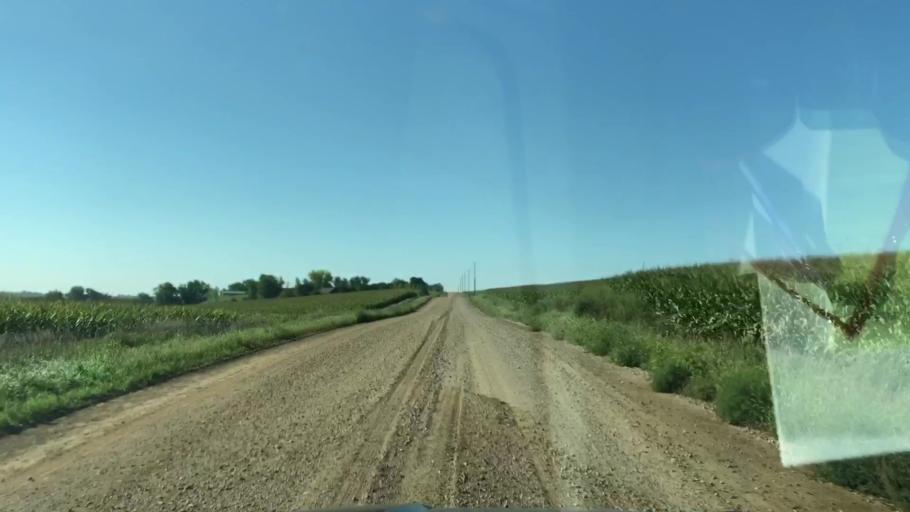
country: US
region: Iowa
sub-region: Woodbury County
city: Sergeant Bluff
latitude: 42.4650
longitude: -96.2526
